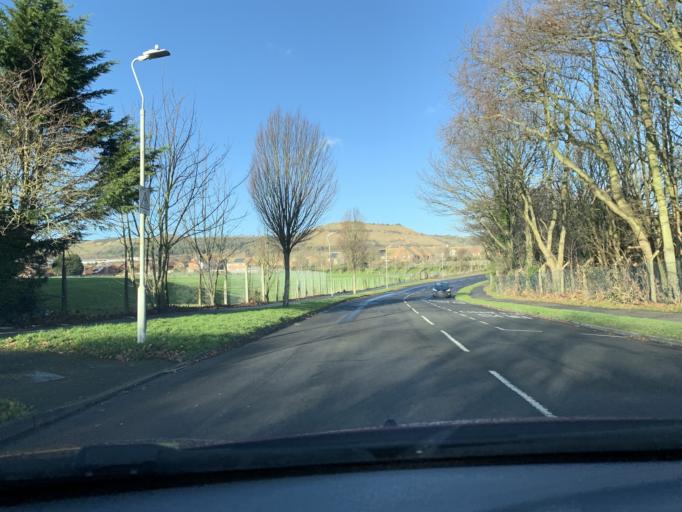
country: GB
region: England
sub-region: Kent
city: Folkestone
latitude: 51.0873
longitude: 1.1636
